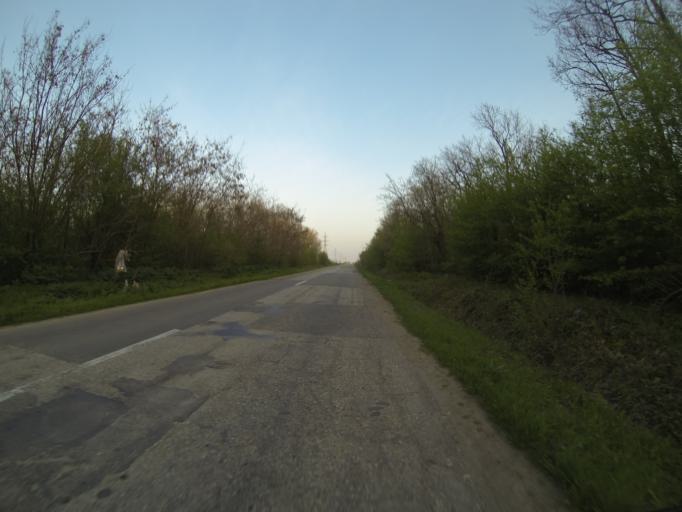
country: RO
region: Dolj
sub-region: Comuna Dranicu
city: Dranic
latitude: 44.0640
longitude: 23.8144
